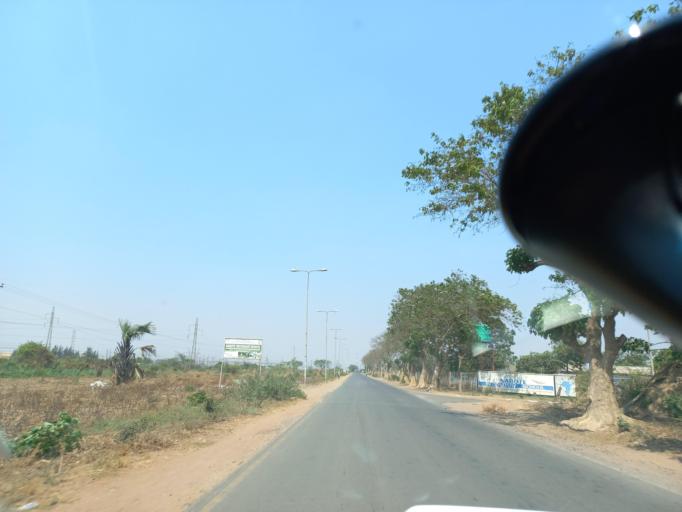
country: ZM
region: Lusaka
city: Kafue
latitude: -15.7470
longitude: 28.1662
